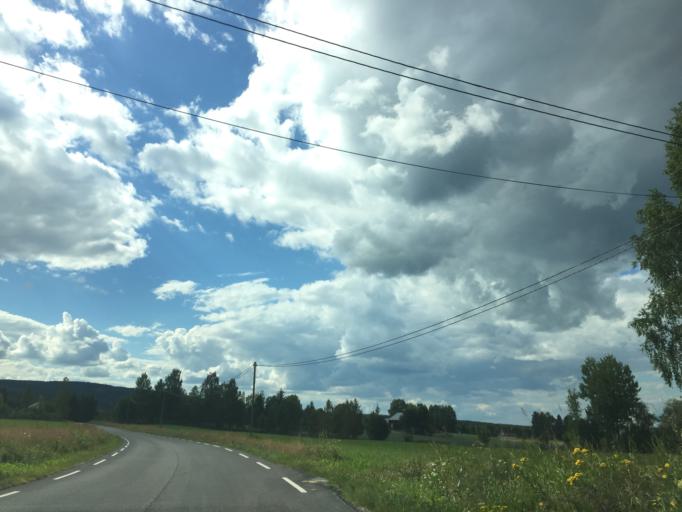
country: NO
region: Hedmark
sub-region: Kongsvinger
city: Spetalen
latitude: 60.1918
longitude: 11.8523
